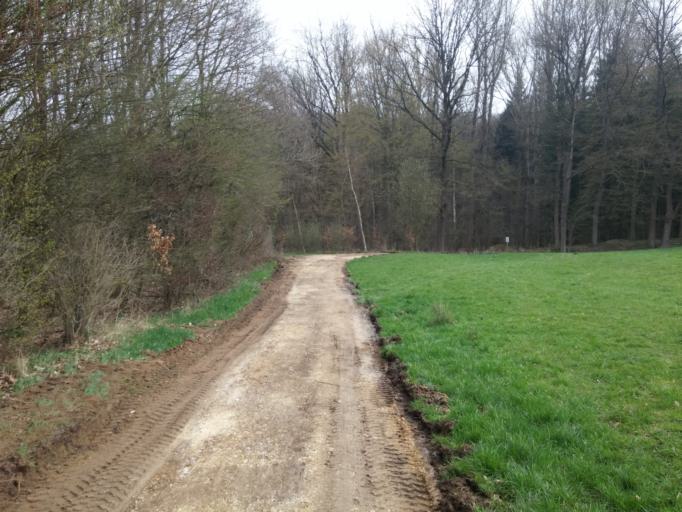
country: DE
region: Baden-Wuerttemberg
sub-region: Regierungsbezirk Stuttgart
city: Wernau
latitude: 48.6963
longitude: 9.4330
